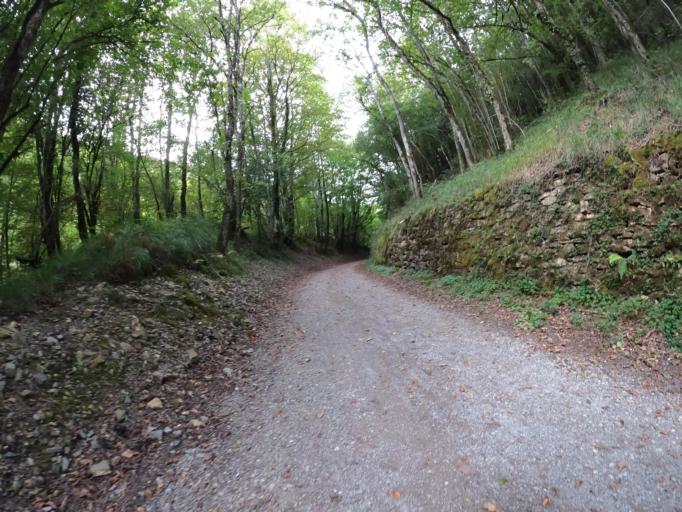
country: ES
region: Navarre
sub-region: Provincia de Navarra
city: Lekunberri
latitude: 42.9819
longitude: -1.8654
